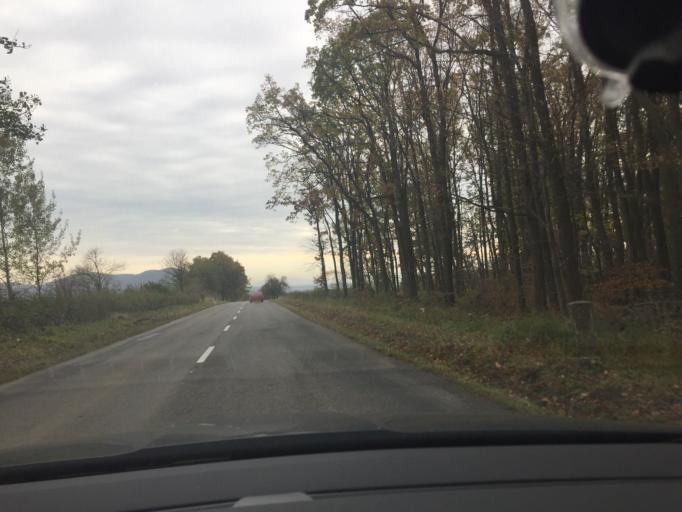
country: SK
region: Presovsky
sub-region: Okres Presov
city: Presov
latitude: 48.9345
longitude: 21.3163
